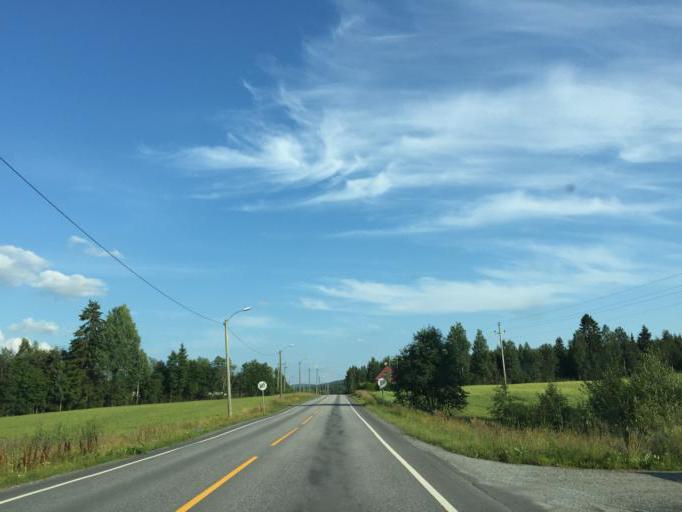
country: NO
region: Hedmark
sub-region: Sor-Odal
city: Skarnes
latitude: 60.2479
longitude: 11.7029
